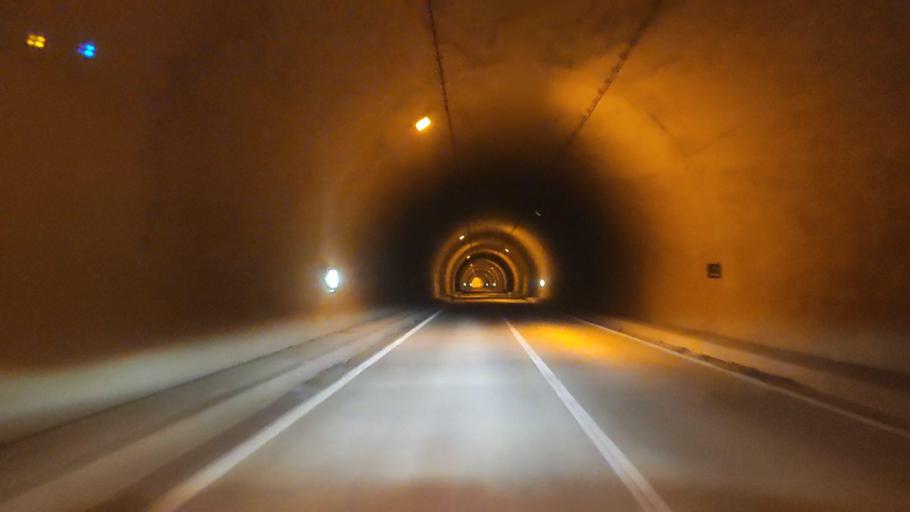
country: JP
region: Kumamoto
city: Matsubase
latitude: 32.5076
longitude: 130.9202
